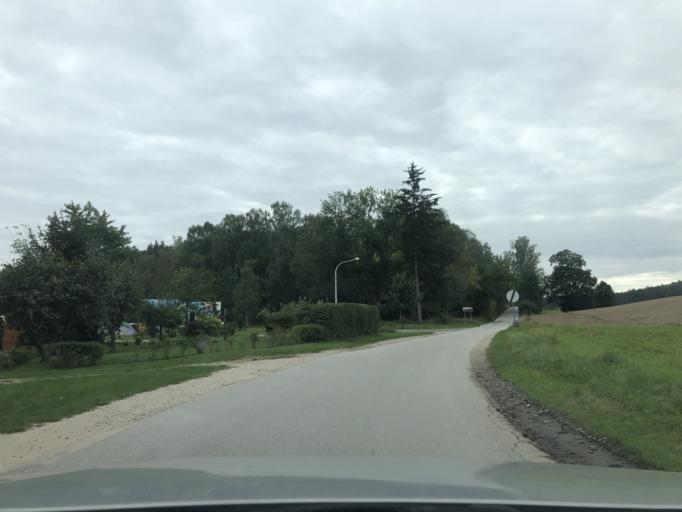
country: PL
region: Greater Poland Voivodeship
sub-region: Powiat pilski
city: Pila
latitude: 53.2646
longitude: 16.6943
